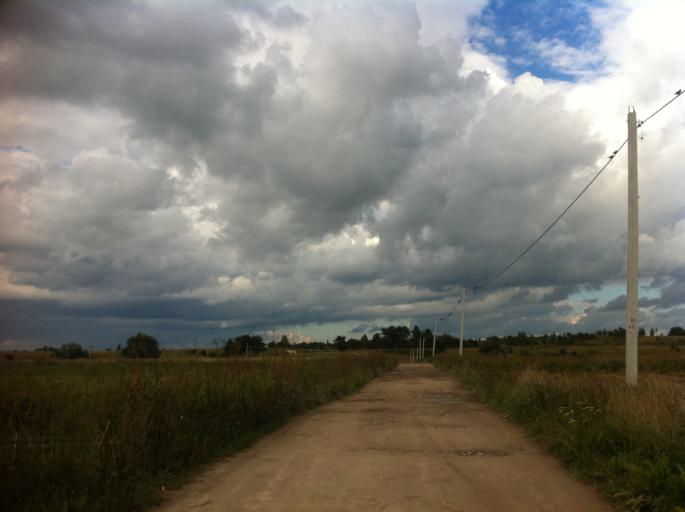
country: RU
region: Pskov
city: Izborsk
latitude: 57.8202
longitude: 27.9619
